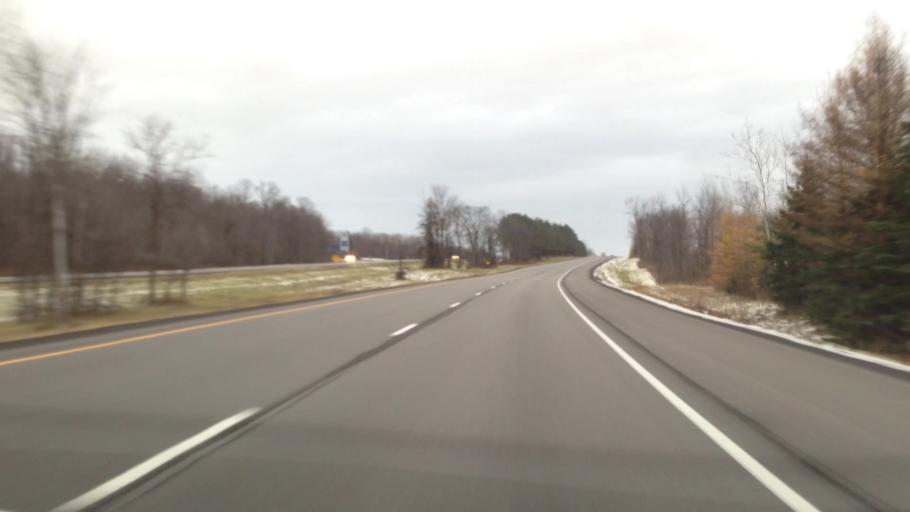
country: CA
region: Quebec
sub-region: Laurentides
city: Brownsburg-Chatham
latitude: 45.5488
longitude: -74.4298
